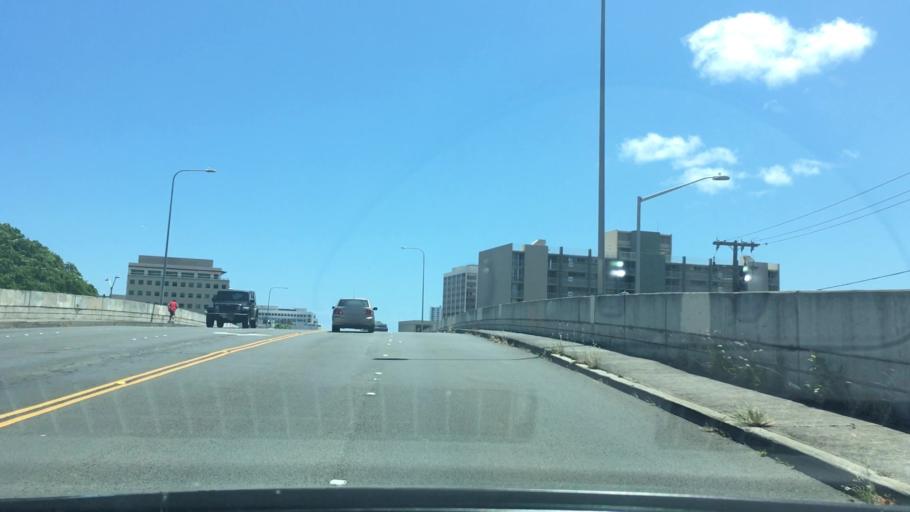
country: US
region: Hawaii
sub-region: Honolulu County
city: Honolulu
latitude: 21.3030
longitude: -157.8379
